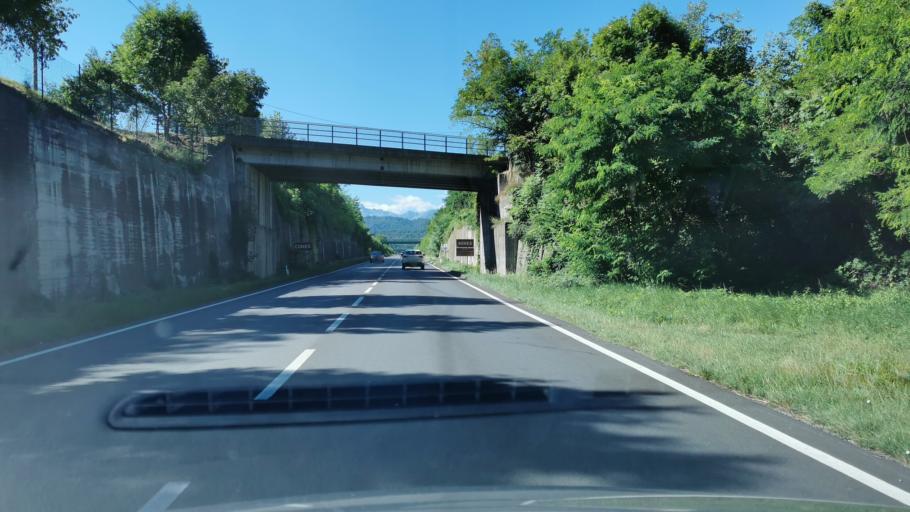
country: IT
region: Piedmont
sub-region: Provincia di Cuneo
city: Boves
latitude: 44.3575
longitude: 7.5487
